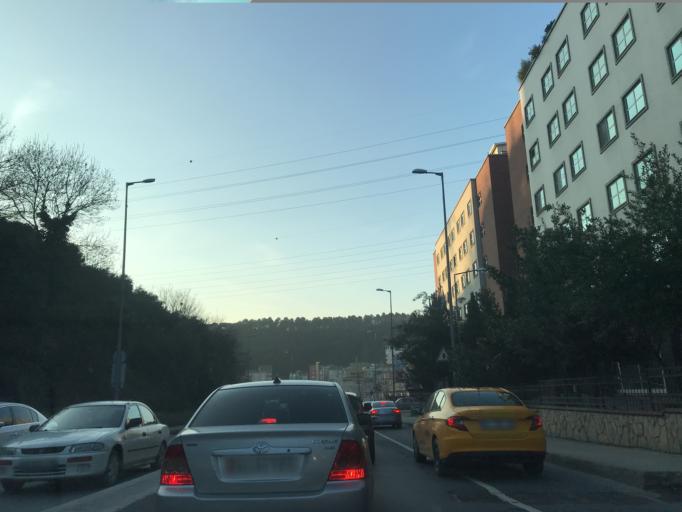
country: TR
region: Istanbul
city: Sisli
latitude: 41.1111
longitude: 29.0000
